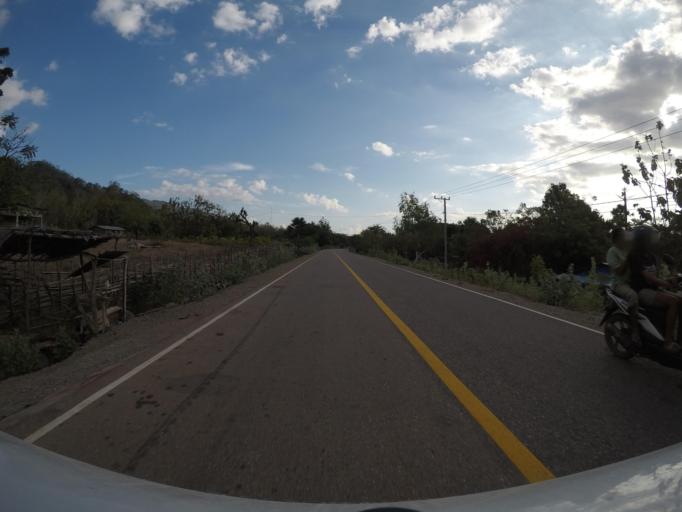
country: TL
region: Bobonaro
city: Maliana
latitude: -8.8859
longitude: 125.0256
